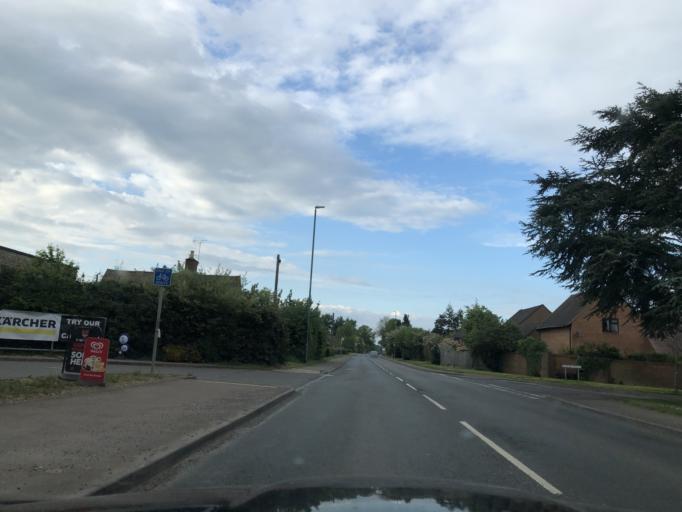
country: GB
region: England
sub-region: Gloucestershire
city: Moreton in Marsh
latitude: 51.9844
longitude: -1.7048
